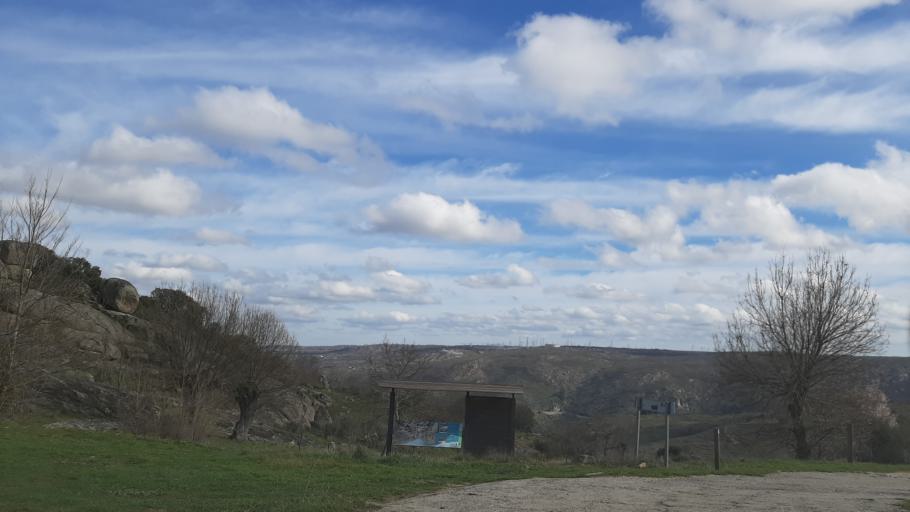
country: ES
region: Castille and Leon
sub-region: Provincia de Salamanca
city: Villarino de los Aires
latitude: 41.2632
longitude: -6.5270
